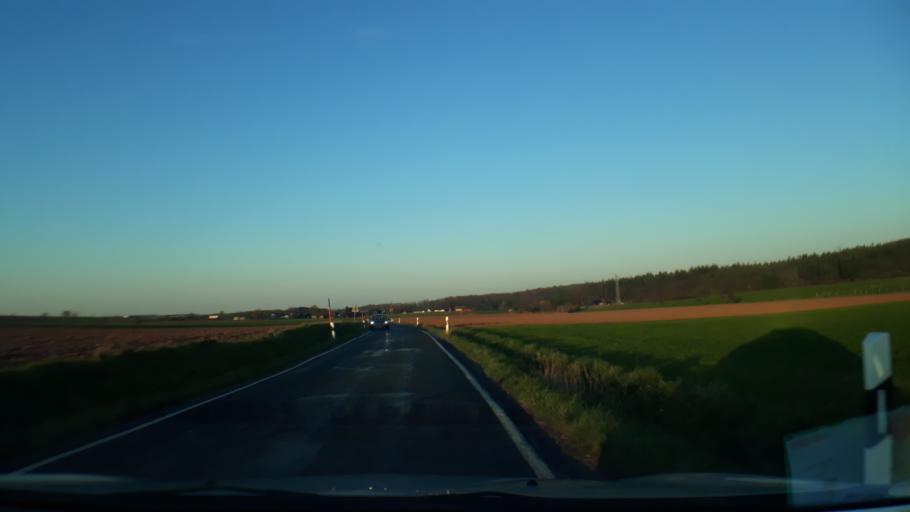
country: DE
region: North Rhine-Westphalia
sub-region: Regierungsbezirk Koln
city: Mechernich
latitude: 50.6186
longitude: 6.6064
